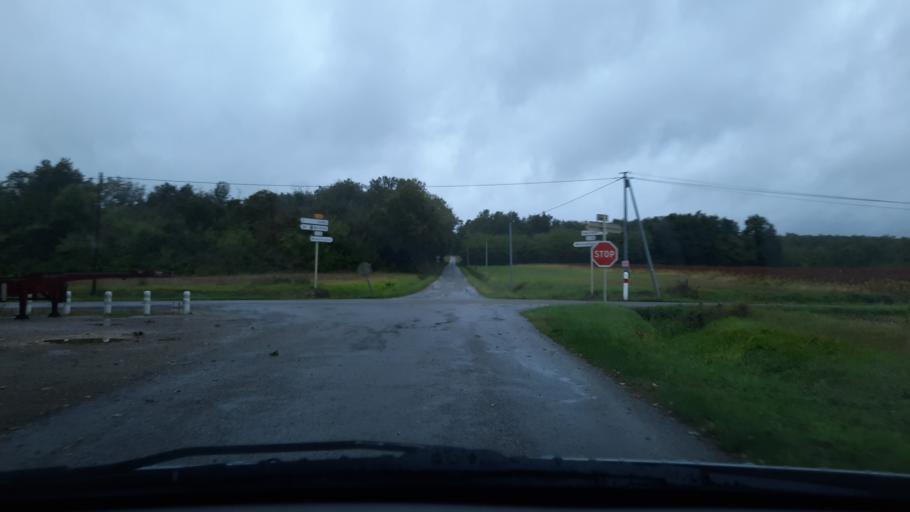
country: FR
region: Midi-Pyrenees
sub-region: Departement du Tarn-et-Garonne
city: Lafrancaise
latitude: 44.1782
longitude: 1.2694
